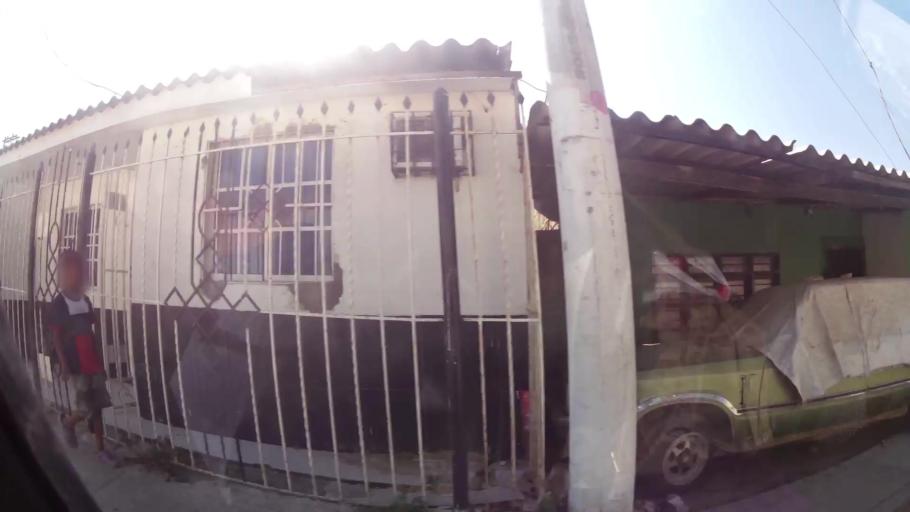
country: CO
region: Atlantico
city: Barranquilla
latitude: 10.9813
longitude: -74.8257
